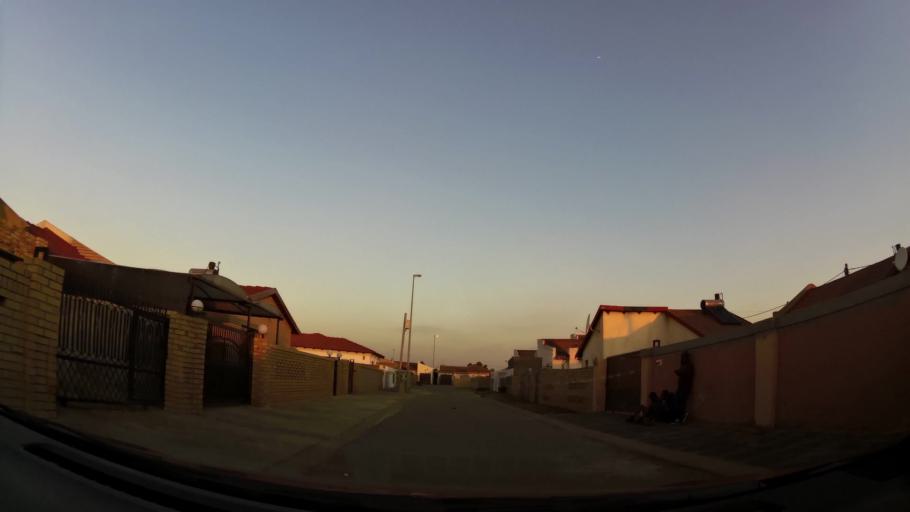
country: ZA
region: Gauteng
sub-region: City of Johannesburg Metropolitan Municipality
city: Soweto
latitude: -26.2255
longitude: 27.8437
